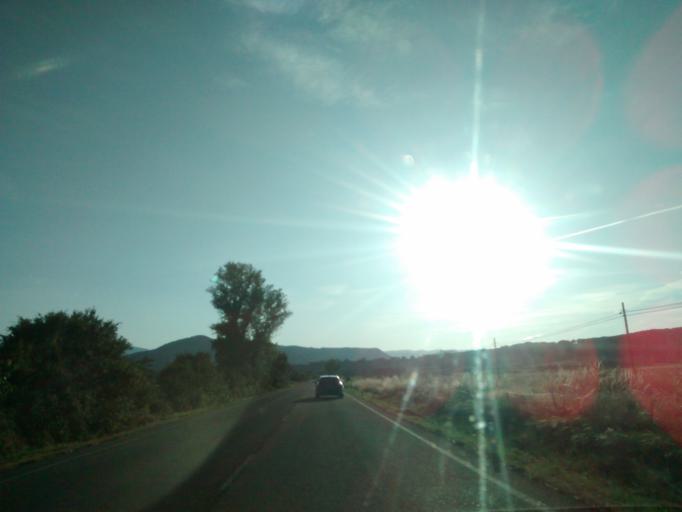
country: ES
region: Aragon
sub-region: Provincia de Huesca
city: Bailo
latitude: 42.5739
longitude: -0.7630
